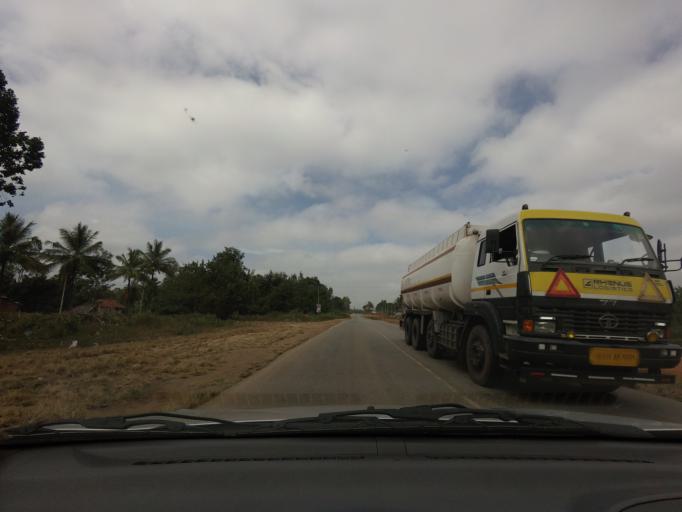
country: IN
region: Karnataka
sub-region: Hassan
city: Alur
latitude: 12.9530
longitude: 75.9236
